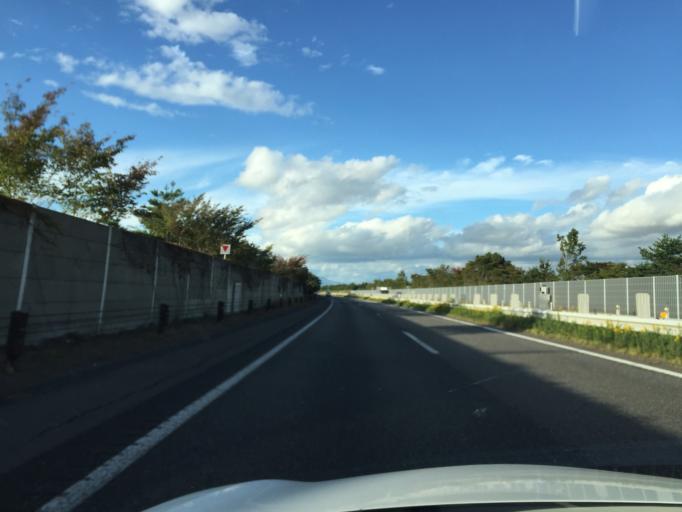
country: JP
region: Fukushima
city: Koriyama
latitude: 37.3805
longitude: 140.3127
